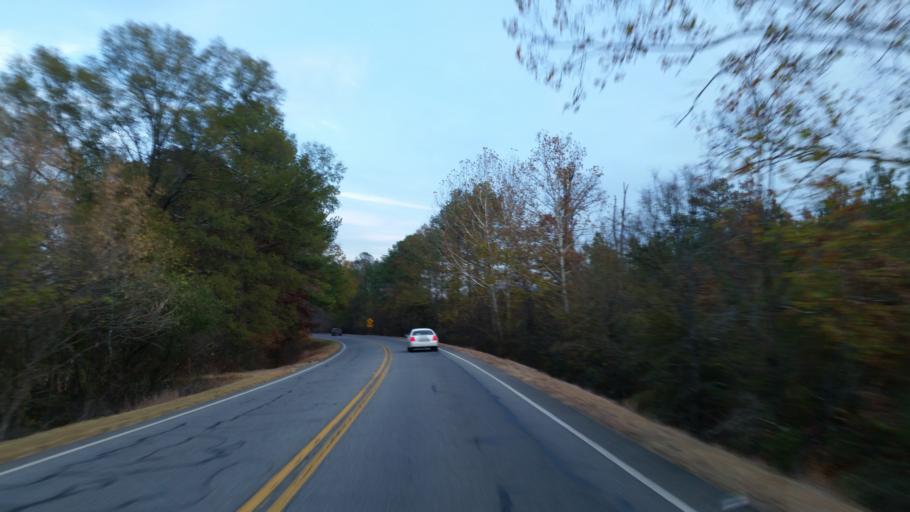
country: US
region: Georgia
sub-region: Murray County
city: Chatsworth
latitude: 34.6009
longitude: -84.7863
